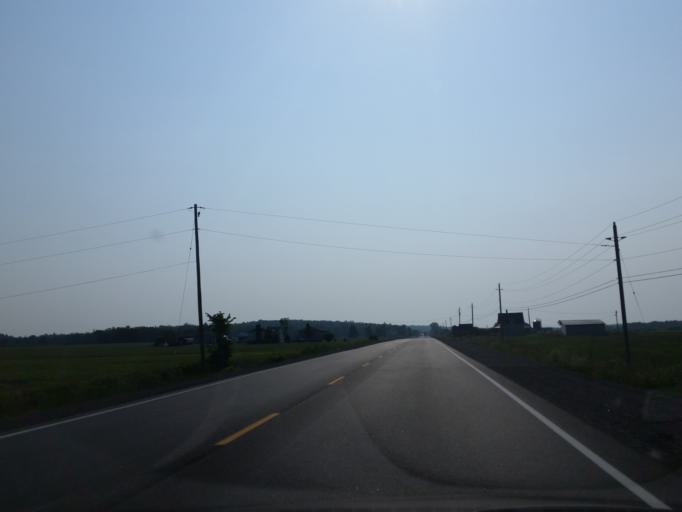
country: CA
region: Ontario
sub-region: Nipissing District
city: North Bay
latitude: 46.4071
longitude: -80.0726
